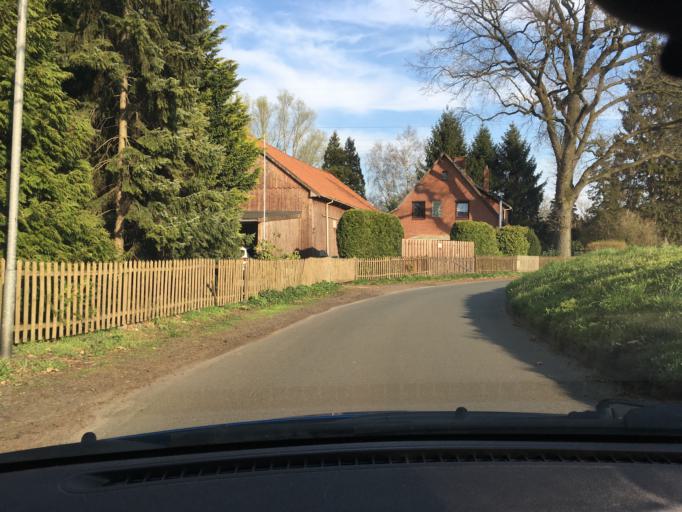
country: DE
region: Lower Saxony
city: Stelle
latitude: 53.4125
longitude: 10.0556
